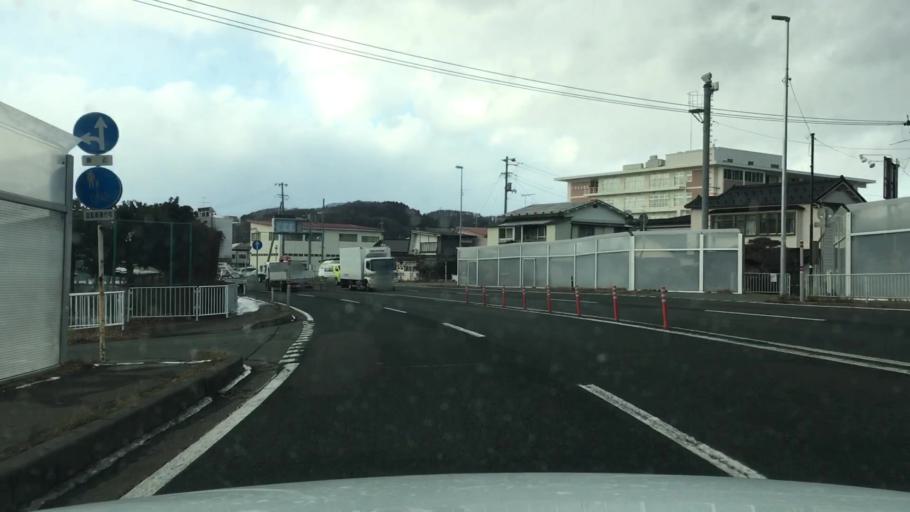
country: JP
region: Iwate
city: Morioka-shi
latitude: 39.7062
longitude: 141.1699
